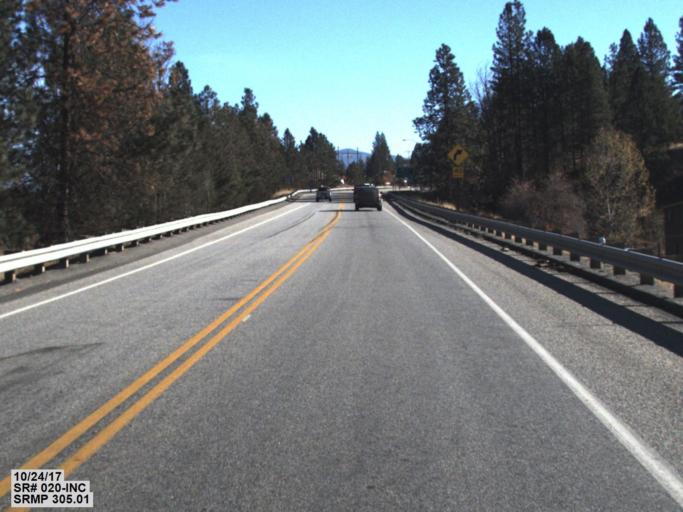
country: US
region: Washington
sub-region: Ferry County
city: Republic
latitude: 48.6511
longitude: -118.6892
